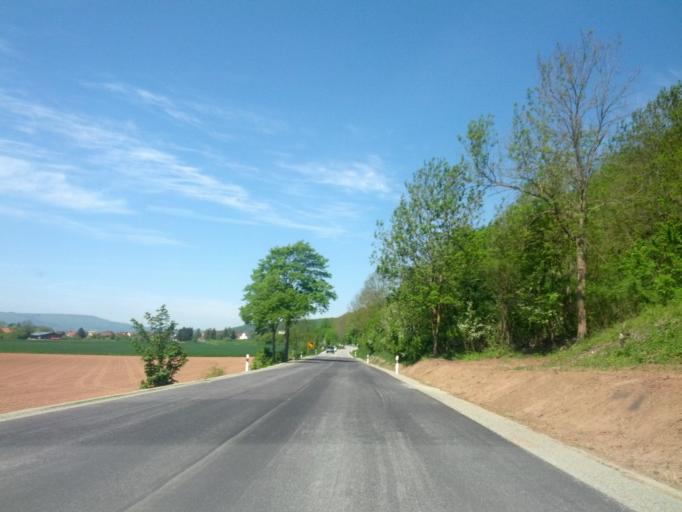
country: DE
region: Thuringia
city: Kella
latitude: 51.1921
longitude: 10.1185
